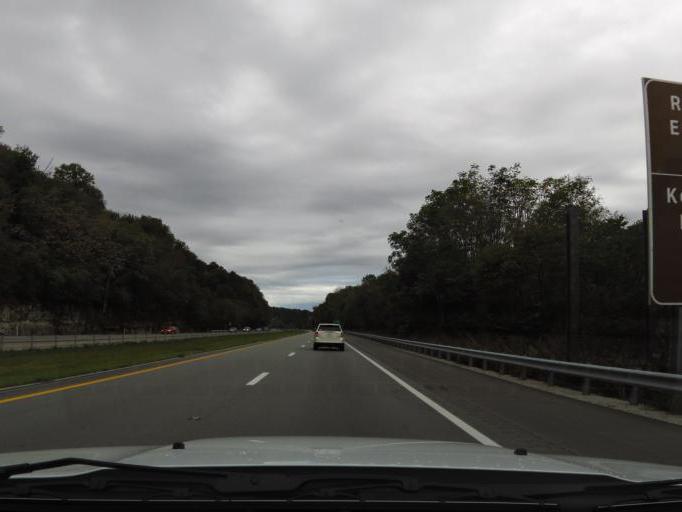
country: US
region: Kentucky
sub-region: Rockcastle County
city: Mount Vernon
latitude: 37.3726
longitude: -84.3211
